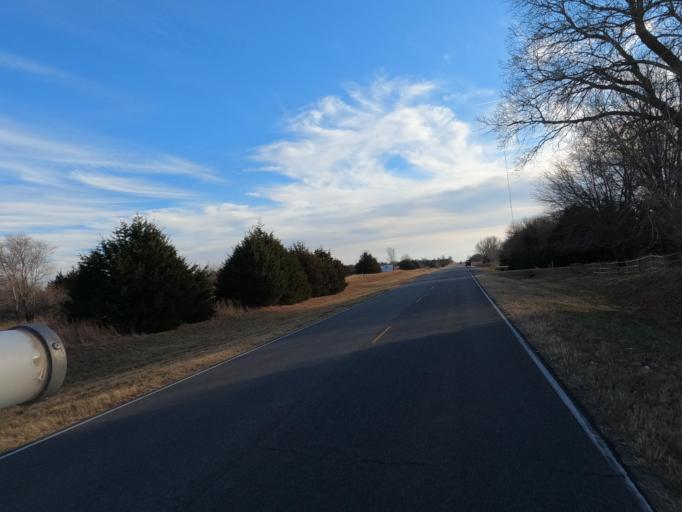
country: US
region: Kansas
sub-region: Reno County
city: Buhler
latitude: 38.0649
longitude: -97.7754
